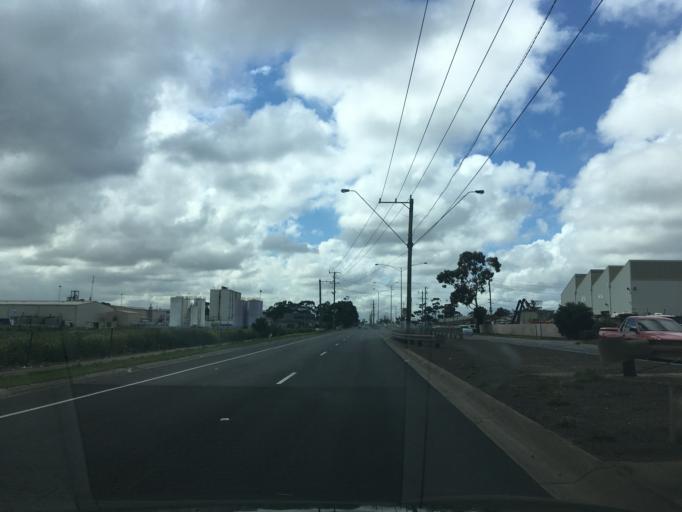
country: AU
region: Victoria
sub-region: Hobsons Bay
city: Laverton
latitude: -37.8393
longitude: 144.7830
